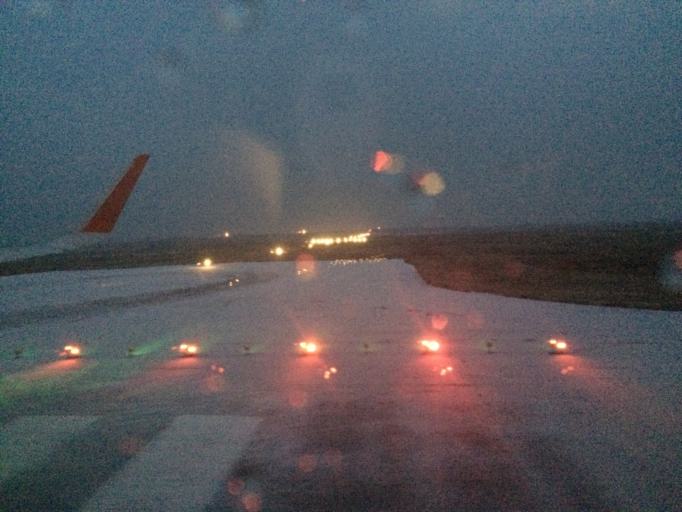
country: RU
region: Novosibirsk
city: Ob'
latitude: 55.0147
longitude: 82.6780
